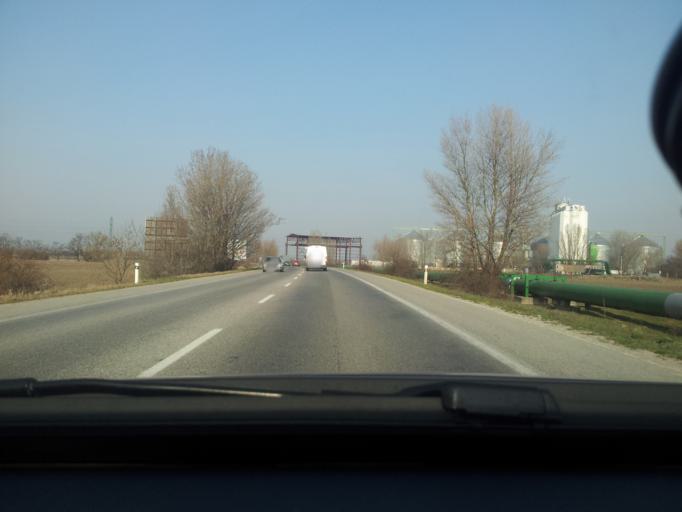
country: SK
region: Trnavsky
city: Leopoldov
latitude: 48.4364
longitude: 17.7508
